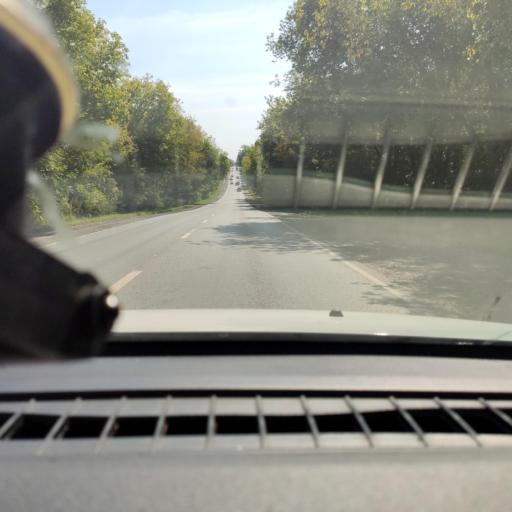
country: RU
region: Samara
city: Novosemeykino
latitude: 53.3219
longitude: 50.2651
